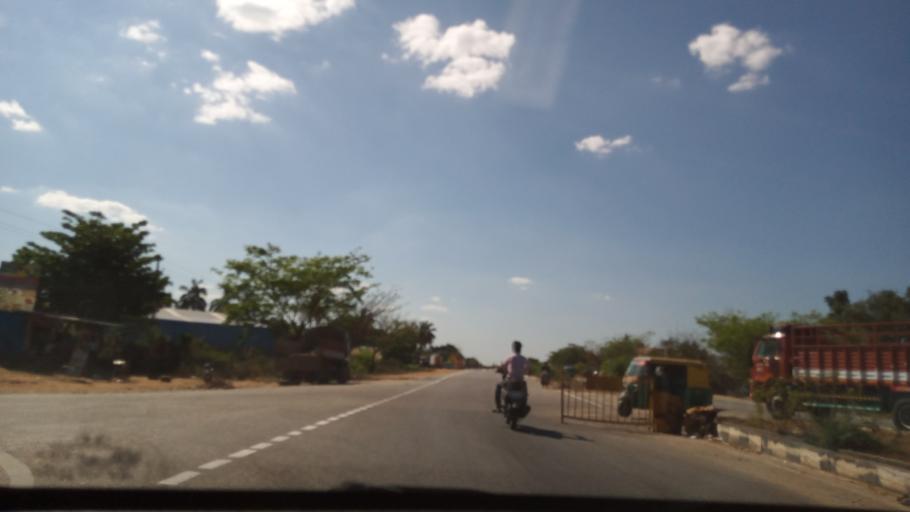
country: IN
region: Karnataka
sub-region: Kolar
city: Mulbagal
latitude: 13.1490
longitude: 78.3890
